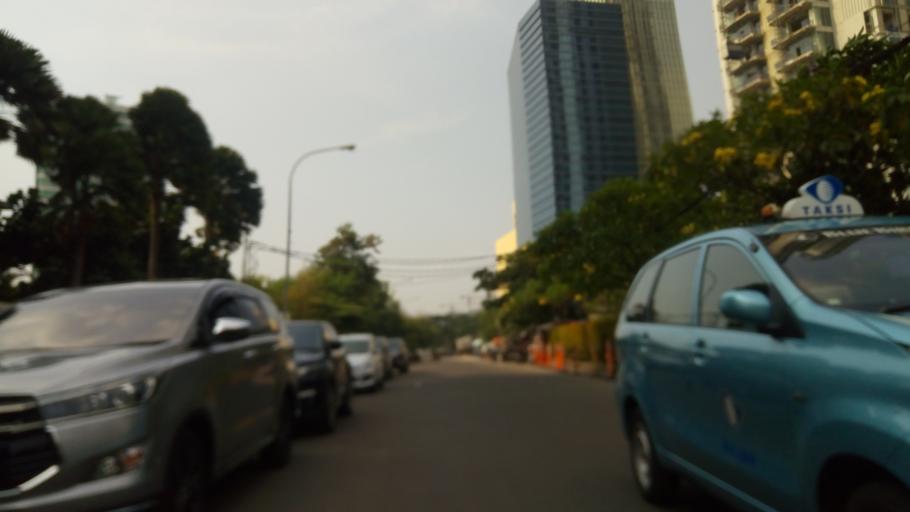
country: ID
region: Jakarta Raya
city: Jakarta
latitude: -6.2145
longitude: 106.8331
